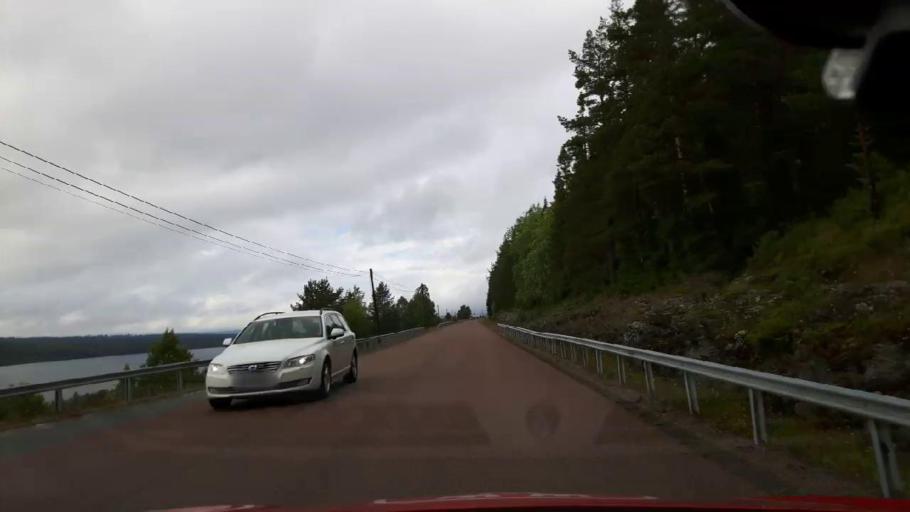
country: SE
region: Jaemtland
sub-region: Krokoms Kommun
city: Valla
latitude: 63.3582
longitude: 14.0770
